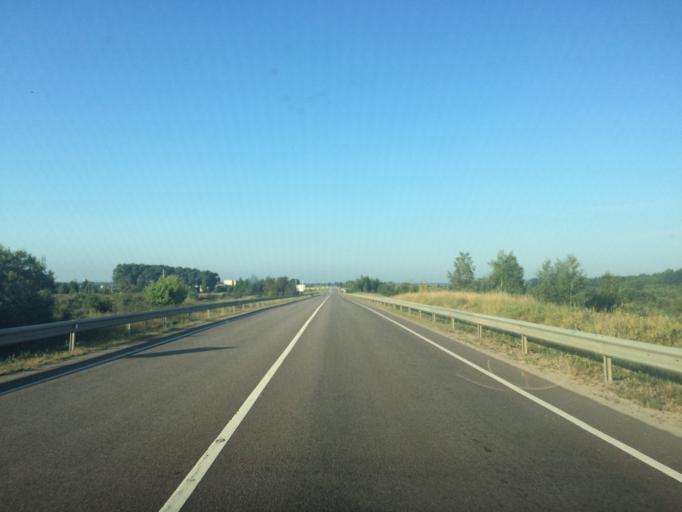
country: LT
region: Vilnius County
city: Ukmerge
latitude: 55.3288
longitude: 24.8835
